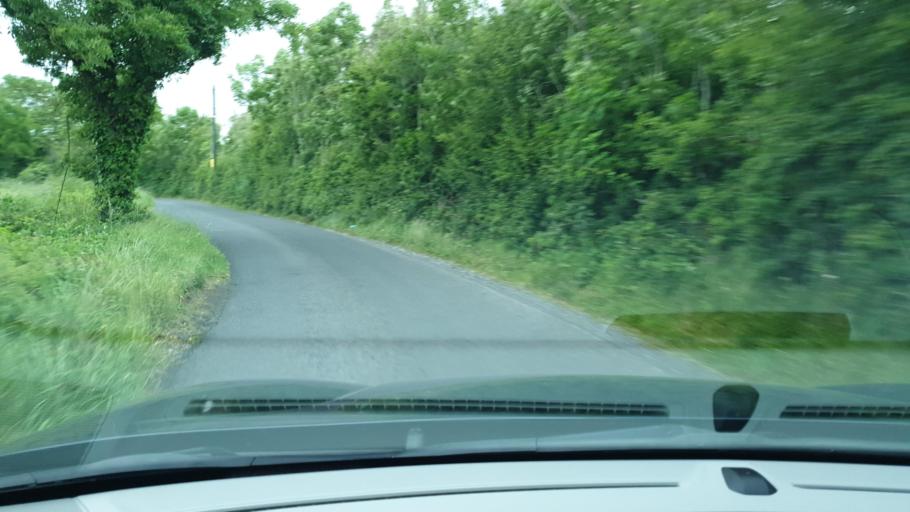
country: IE
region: Leinster
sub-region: An Mhi
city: Navan
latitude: 53.6411
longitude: -6.7210
